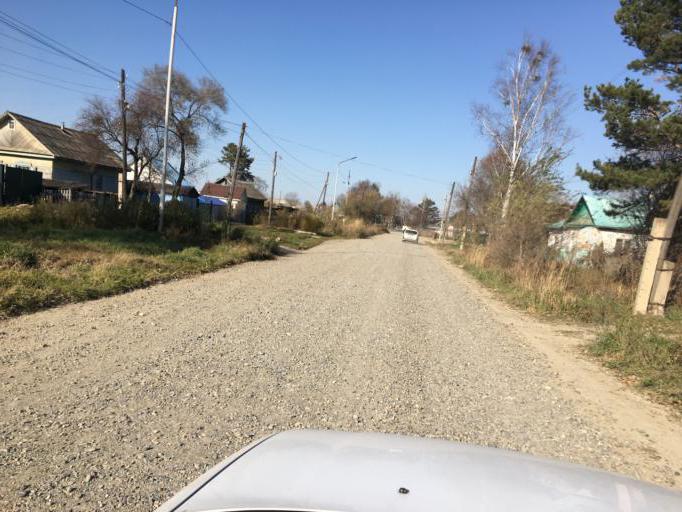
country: RU
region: Primorskiy
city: Dal'nerechensk
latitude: 45.9188
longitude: 133.7162
